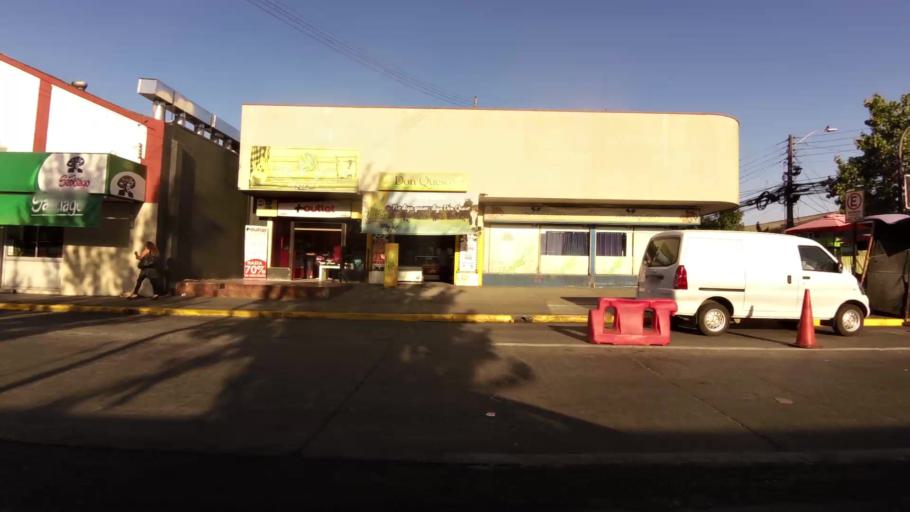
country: CL
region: Maule
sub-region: Provincia de Talca
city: Talca
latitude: -35.4295
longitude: -71.6479
